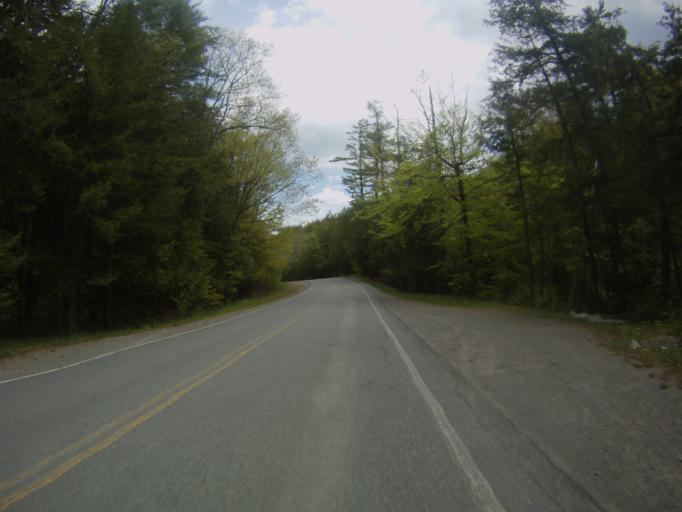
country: US
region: New York
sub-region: Essex County
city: Port Henry
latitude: 43.9428
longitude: -73.4837
